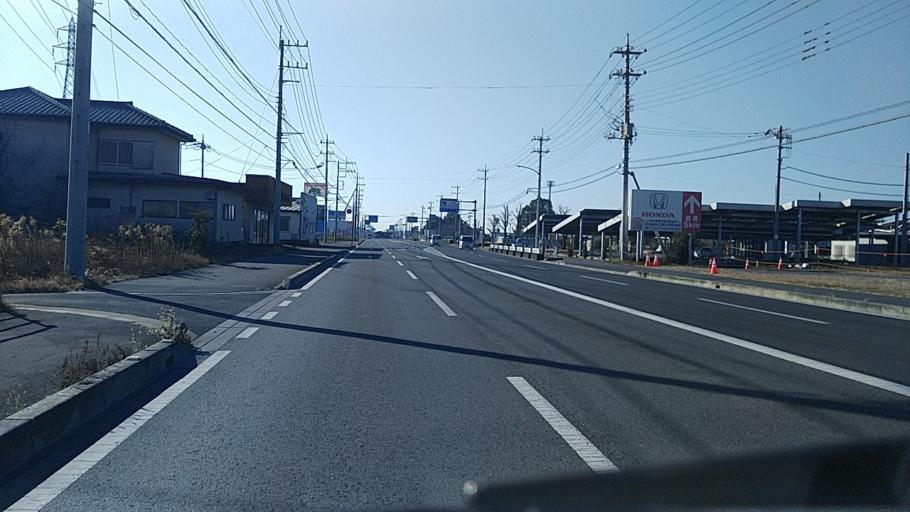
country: JP
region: Tochigi
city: Tanuma
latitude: 36.3450
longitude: 139.5735
